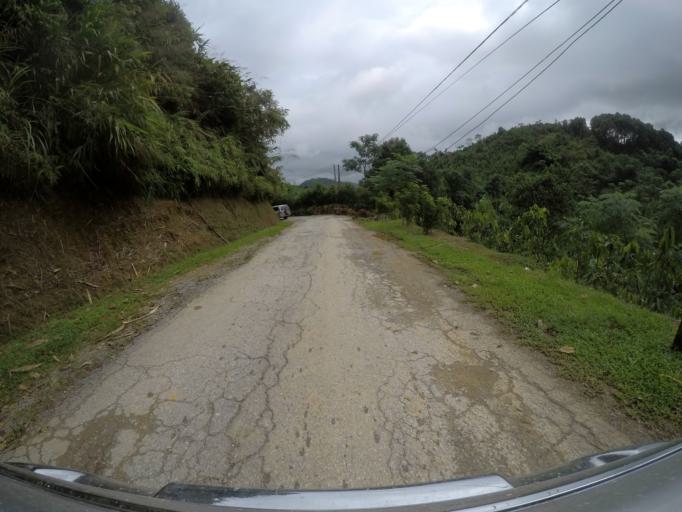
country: VN
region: Yen Bai
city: Co Phuc
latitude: 21.8171
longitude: 104.6239
